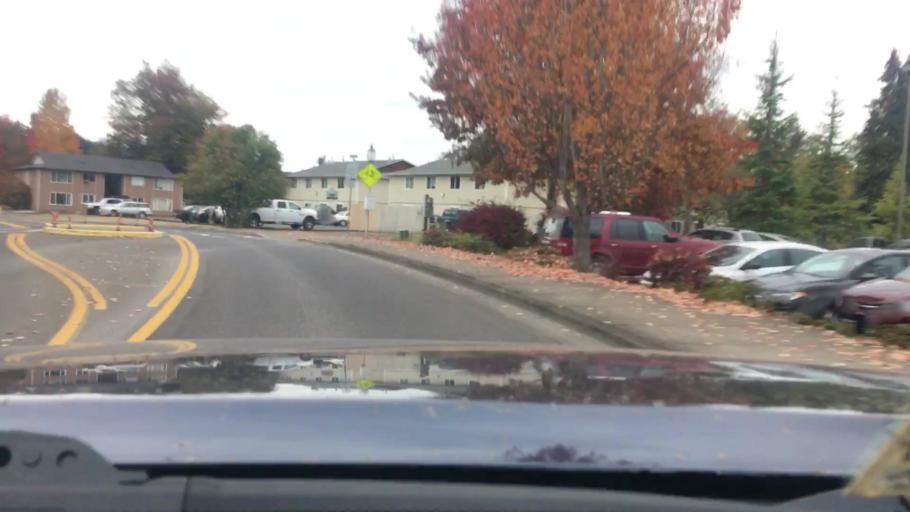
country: US
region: Oregon
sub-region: Lane County
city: Cottage Grove
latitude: 43.7999
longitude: -123.0486
